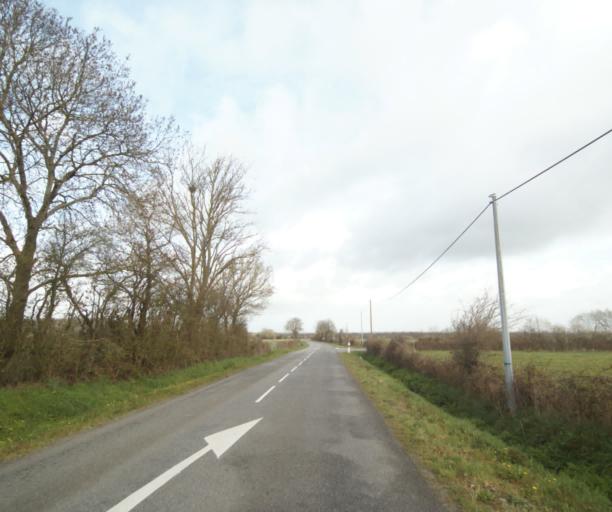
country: FR
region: Pays de la Loire
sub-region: Departement de la Loire-Atlantique
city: Bouvron
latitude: 47.4113
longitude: -1.8896
